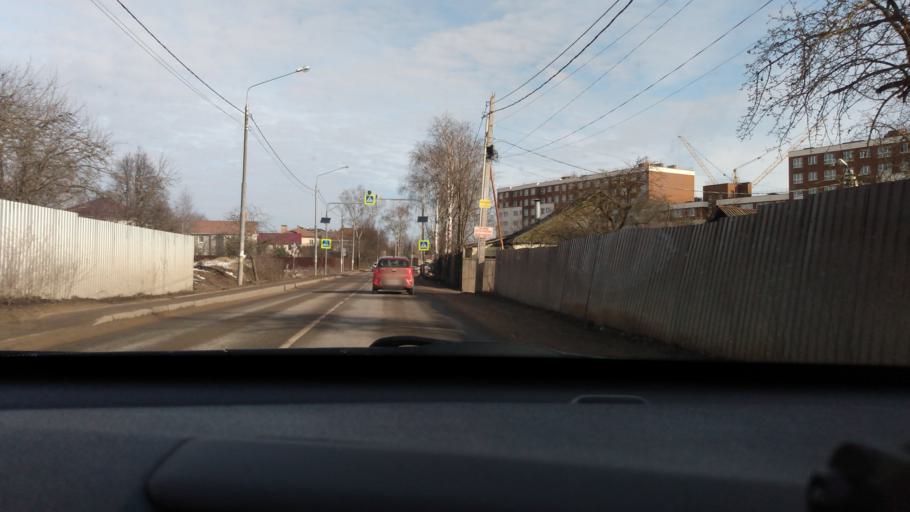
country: RU
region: Moskovskaya
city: Nakhabino
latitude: 55.8550
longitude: 37.1787
